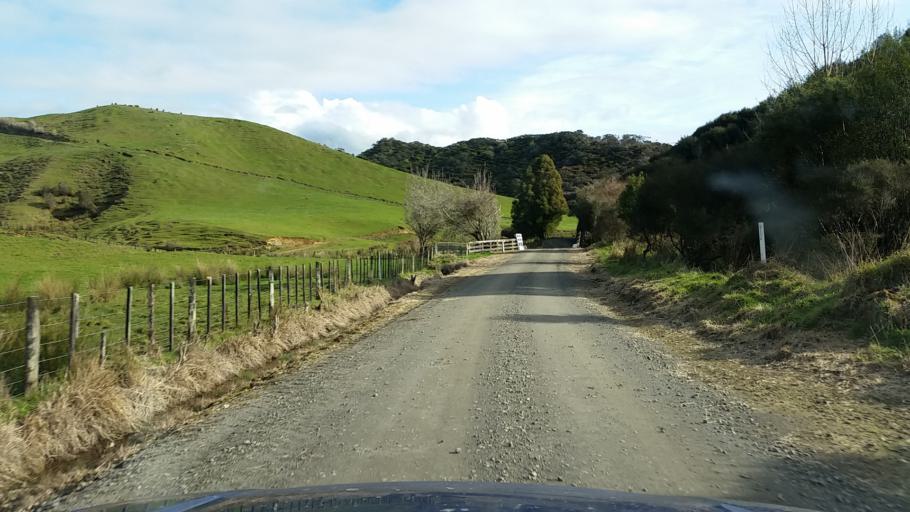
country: NZ
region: Taranaki
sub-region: South Taranaki District
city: Eltham
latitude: -39.2608
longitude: 174.5836
